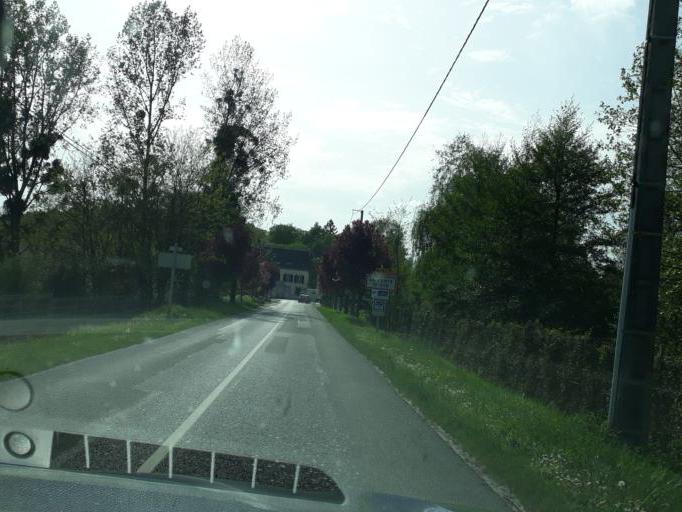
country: FR
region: Centre
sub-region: Departement du Loir-et-Cher
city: Dhuizon
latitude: 47.6590
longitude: 1.6742
